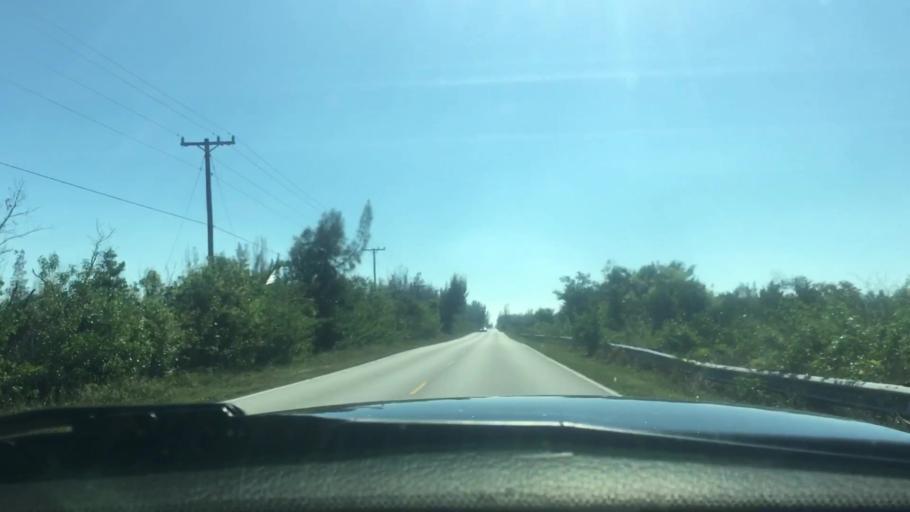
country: US
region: Florida
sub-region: Miami-Dade County
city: Florida City
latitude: 25.4240
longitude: -80.4670
